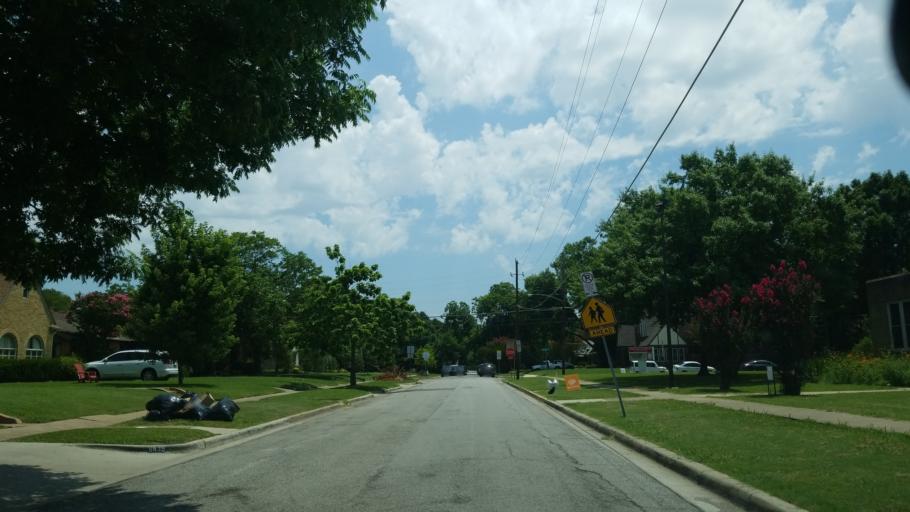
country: US
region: Texas
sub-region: Dallas County
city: Highland Park
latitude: 32.8249
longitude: -96.7667
